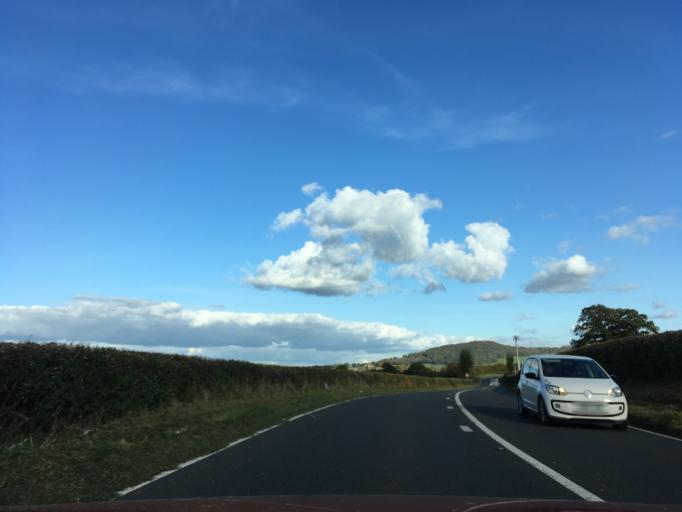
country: GB
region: Wales
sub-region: Sir Powys
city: Hay
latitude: 52.0677
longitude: -3.1478
